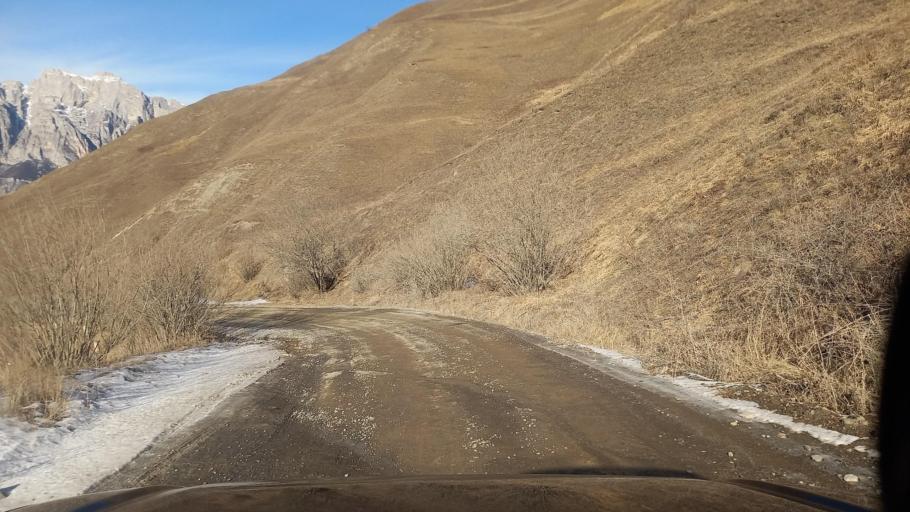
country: RU
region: North Ossetia
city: Verkhniy Fiagdon
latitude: 42.8359
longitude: 44.4748
